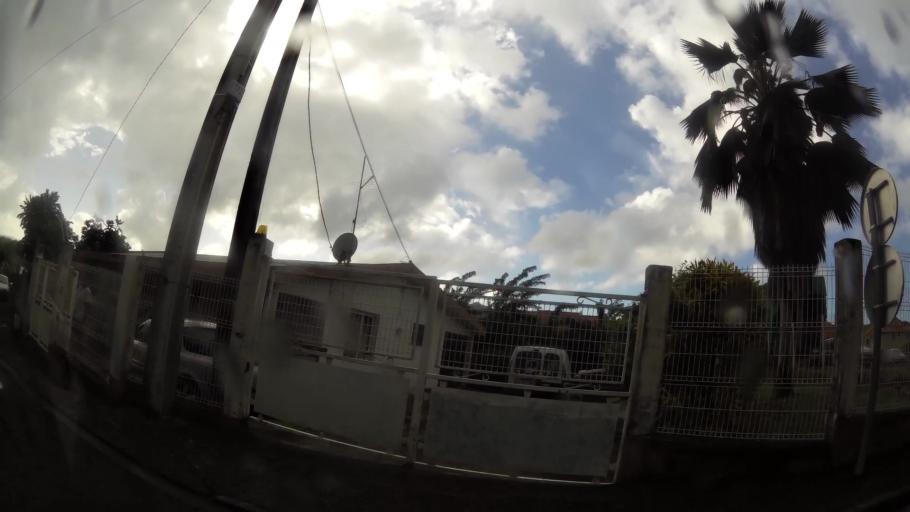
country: MQ
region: Martinique
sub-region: Martinique
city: Les Trois-Ilets
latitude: 14.5385
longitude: -61.0329
